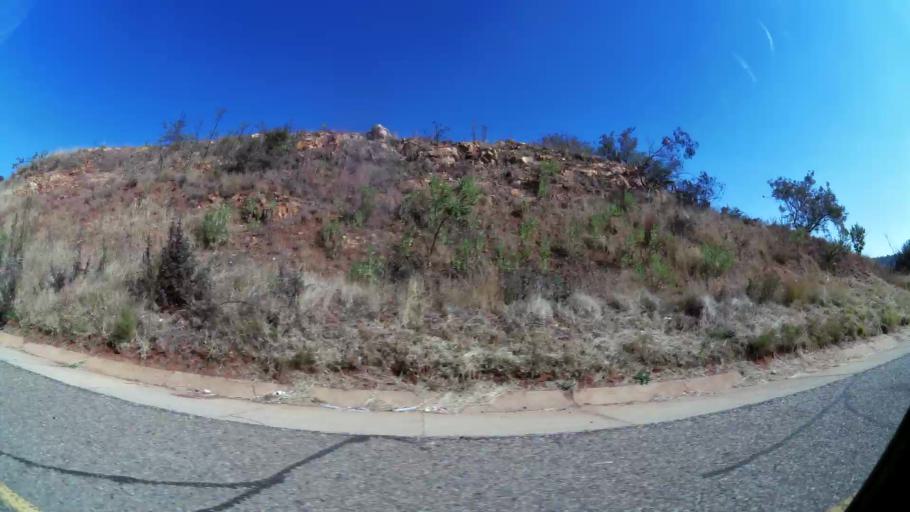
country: ZA
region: Gauteng
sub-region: City of Johannesburg Metropolitan Municipality
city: Roodepoort
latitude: -26.1574
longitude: 27.9272
